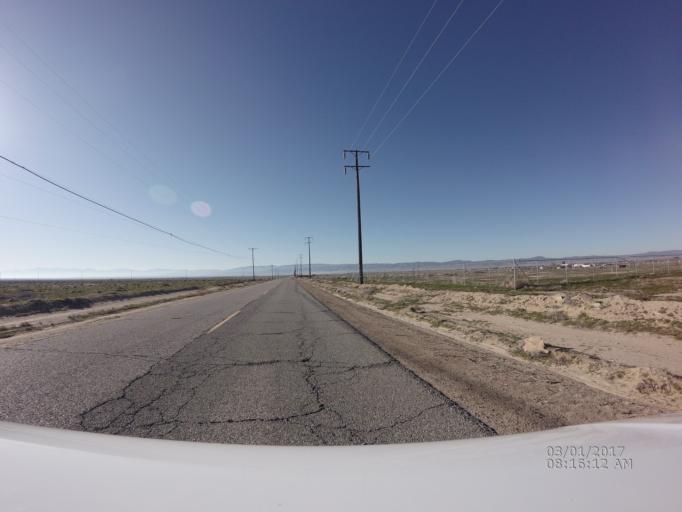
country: US
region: California
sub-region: Los Angeles County
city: Quartz Hill
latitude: 34.7648
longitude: -118.2548
